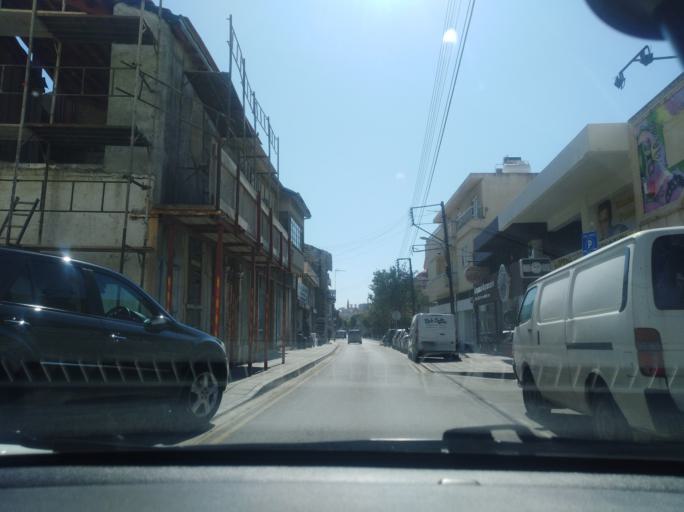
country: CY
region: Limassol
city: Limassol
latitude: 34.6765
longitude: 33.0416
